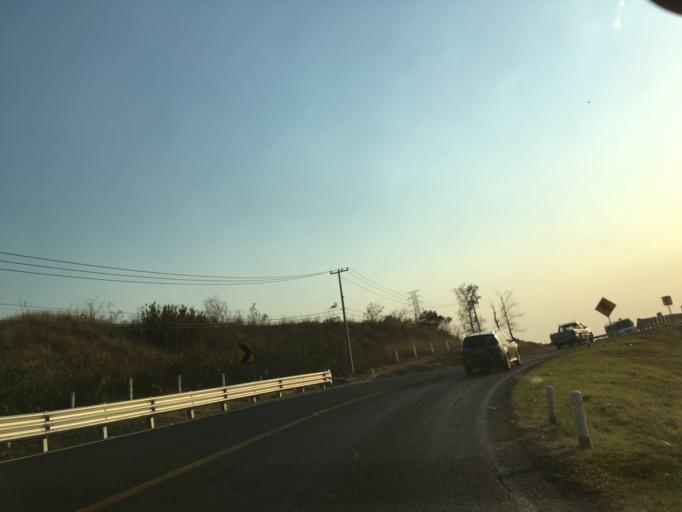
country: MX
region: Michoacan
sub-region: Morelia
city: La Aldea
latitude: 19.7351
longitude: -101.1209
